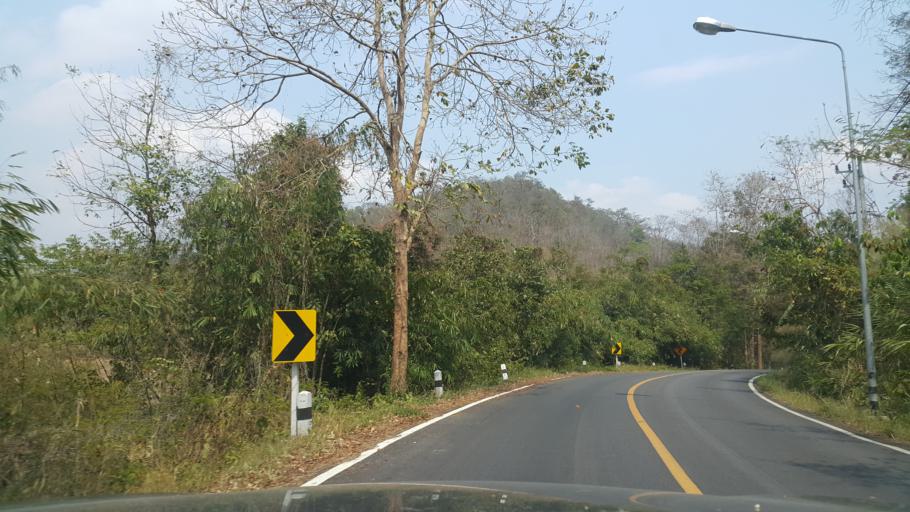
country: TH
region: Lamphun
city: Thung Hua Chang
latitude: 17.9057
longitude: 99.1390
